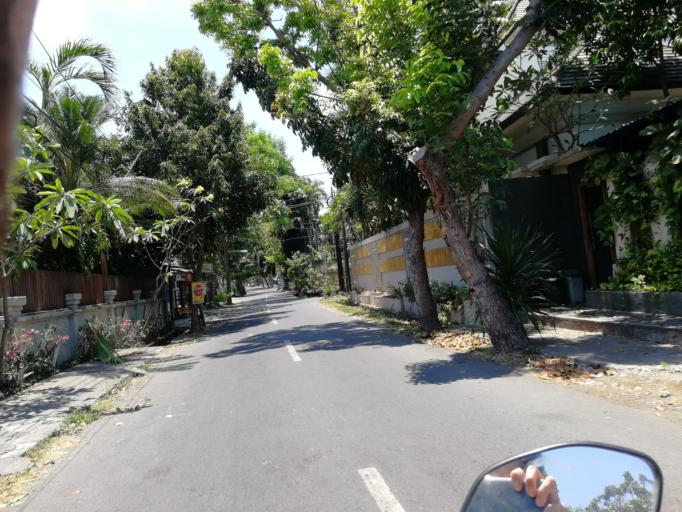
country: ID
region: Bali
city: Dajan Tangluk
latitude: -8.6656
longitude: 115.2367
